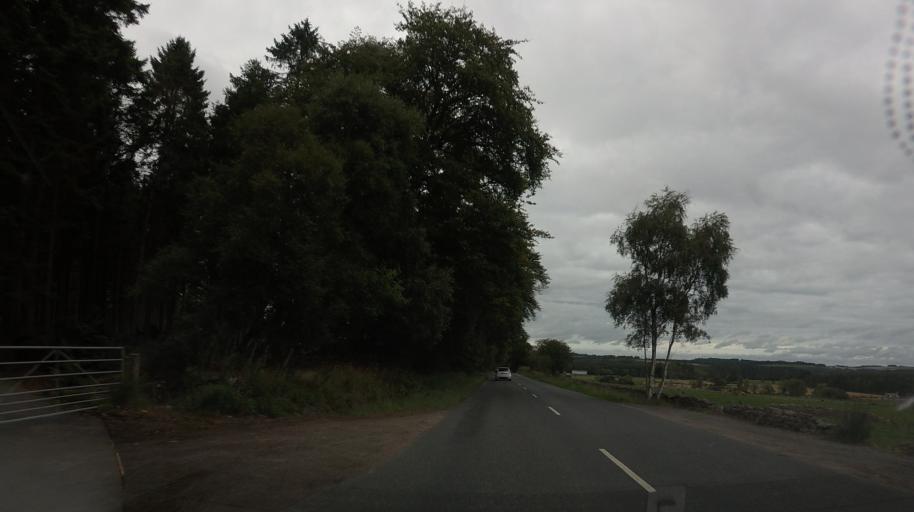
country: GB
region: Scotland
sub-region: Aberdeenshire
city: Banchory
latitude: 57.1229
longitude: -2.4260
